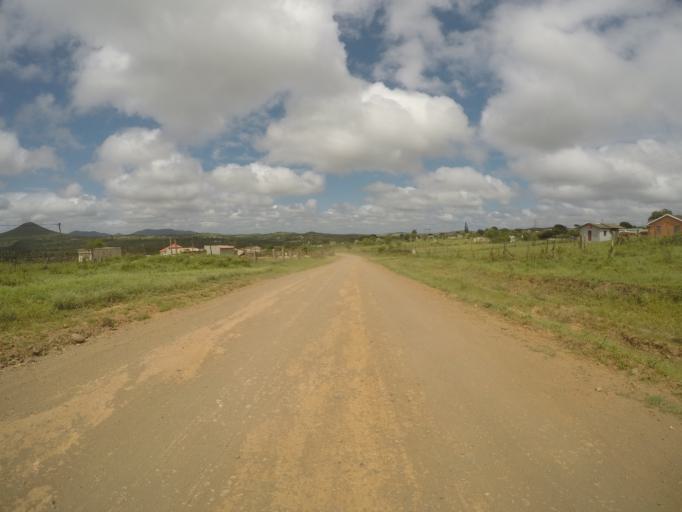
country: ZA
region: KwaZulu-Natal
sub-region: uThungulu District Municipality
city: Empangeni
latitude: -28.5807
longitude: 31.8469
